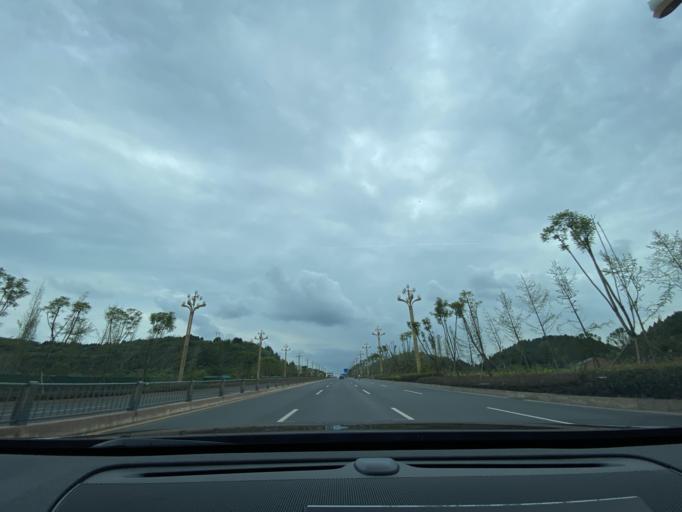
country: CN
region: Sichuan
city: Jiancheng
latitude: 30.4532
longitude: 104.4958
